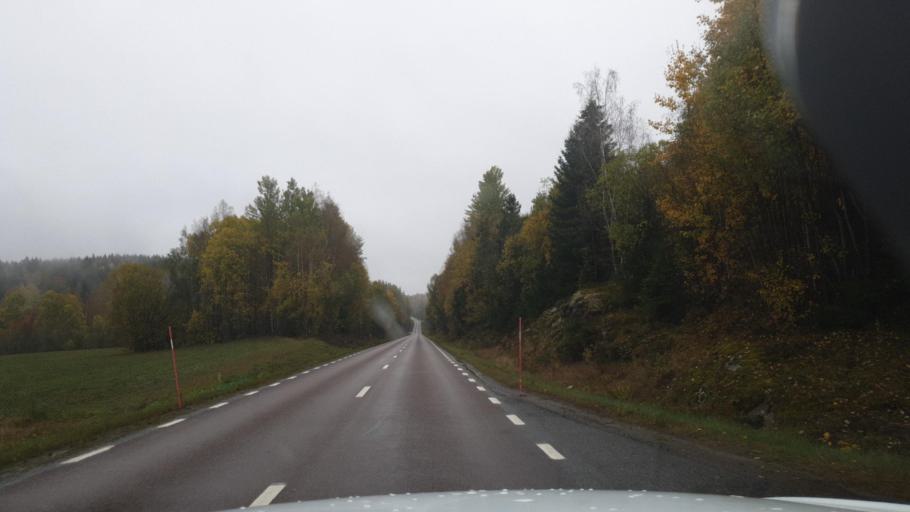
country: SE
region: Vaermland
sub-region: Eda Kommun
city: Amotfors
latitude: 59.7091
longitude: 12.2966
